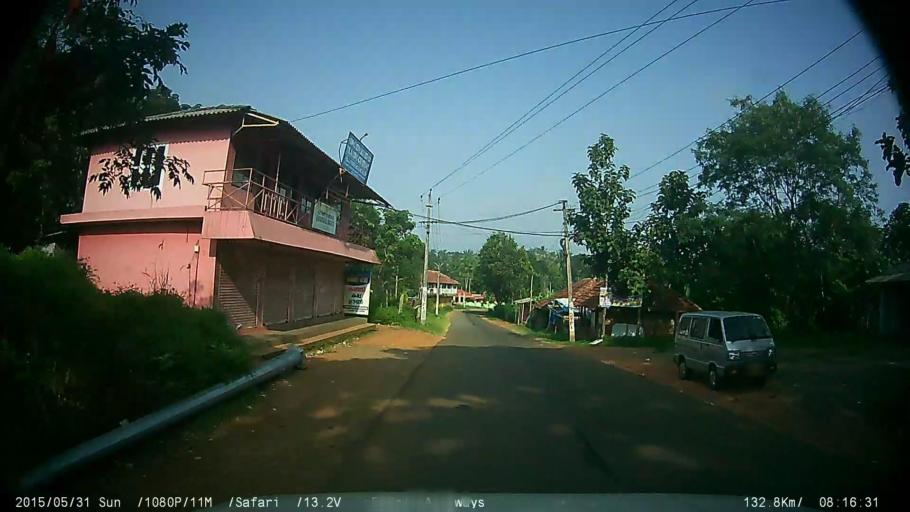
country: IN
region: Kerala
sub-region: Wayanad
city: Kalpetta
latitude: 11.6544
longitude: 75.9956
